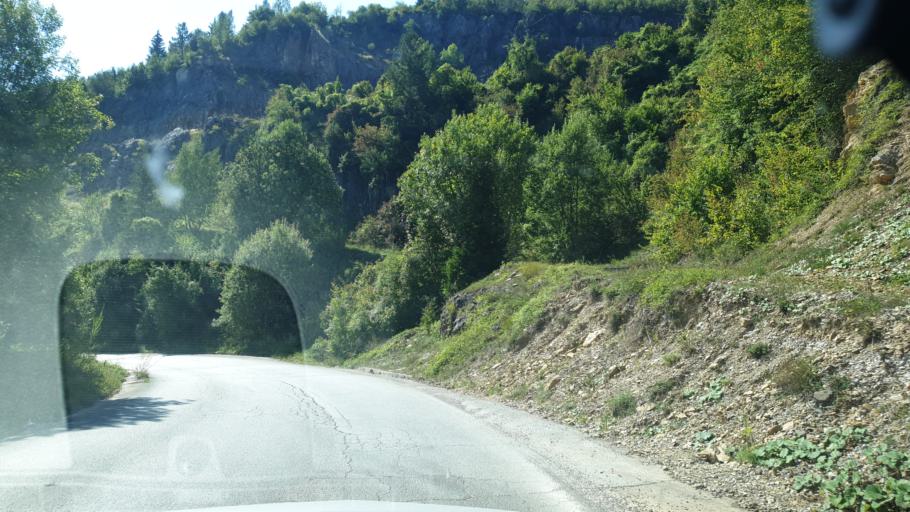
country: RS
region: Central Serbia
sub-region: Zlatiborski Okrug
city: Nova Varos
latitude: 43.4196
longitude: 19.9238
